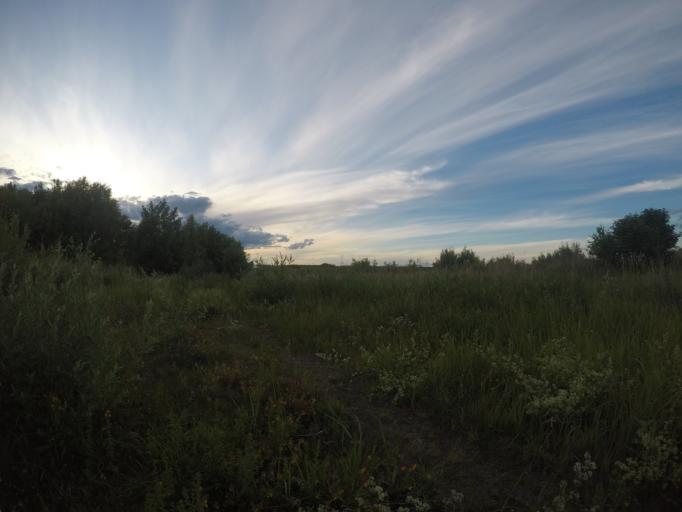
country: SE
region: Stockholm
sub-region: Sigtuna Kommun
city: Rosersberg
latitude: 59.6558
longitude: 17.9607
